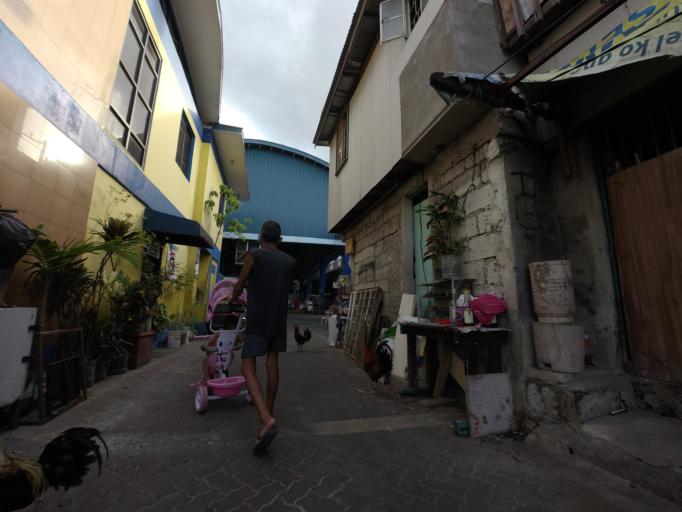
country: PH
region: Metro Manila
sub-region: Mandaluyong
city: Mandaluyong City
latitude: 14.5685
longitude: 121.0402
